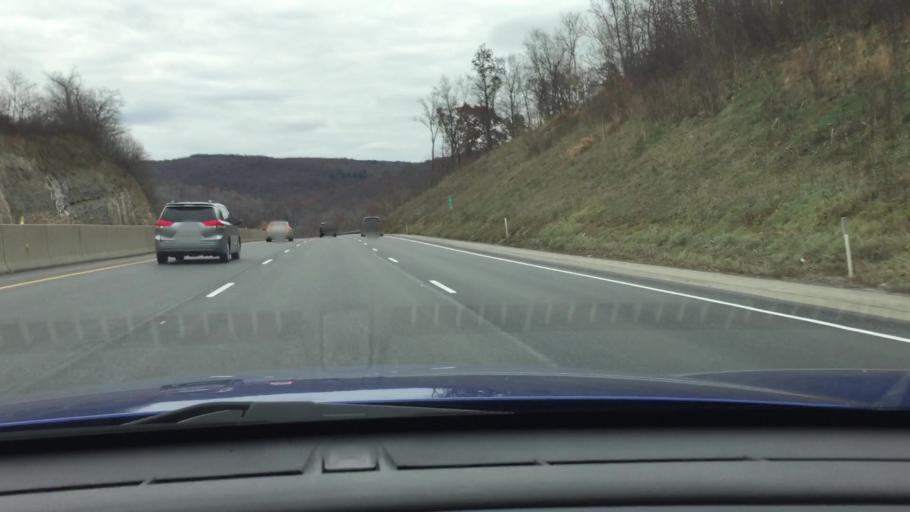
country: US
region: Pennsylvania
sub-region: Fayette County
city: Bear Rocks
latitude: 40.1562
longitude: -79.4749
